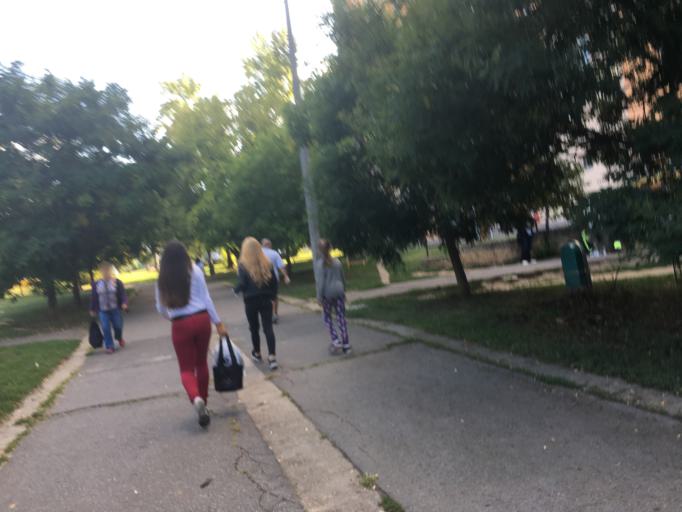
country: HU
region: Budapest
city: Budapest XVII. keruelet
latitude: 47.4816
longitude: 19.2381
